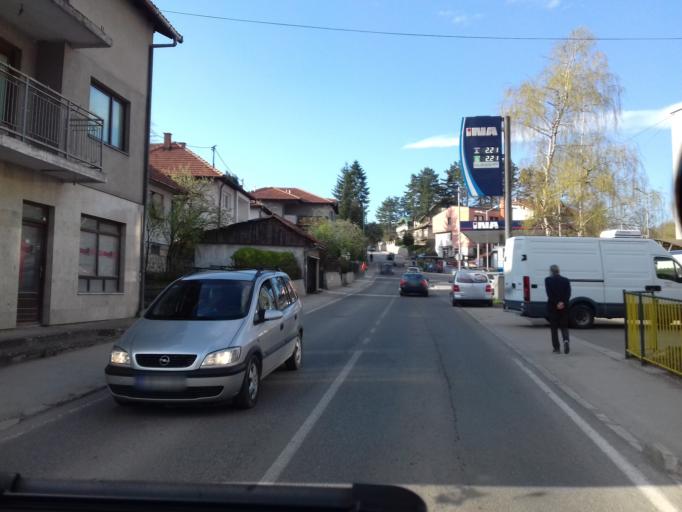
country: BA
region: Federation of Bosnia and Herzegovina
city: Tesanj
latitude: 44.6071
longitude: 17.9869
